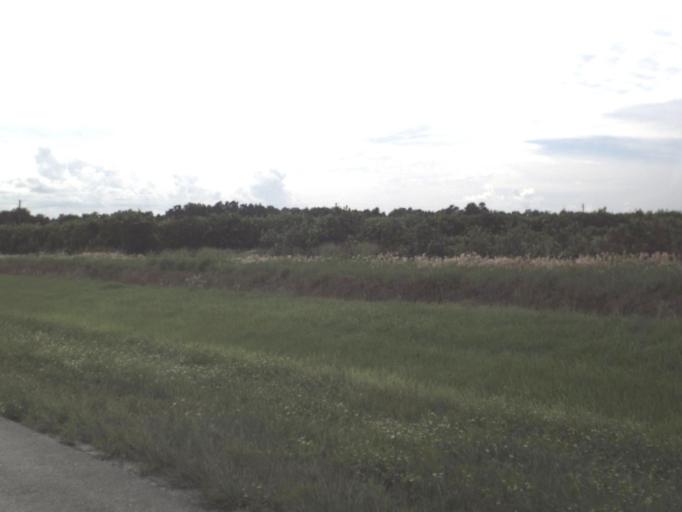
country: US
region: Florida
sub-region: DeSoto County
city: Southeast Arcadia
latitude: 27.1961
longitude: -81.8281
